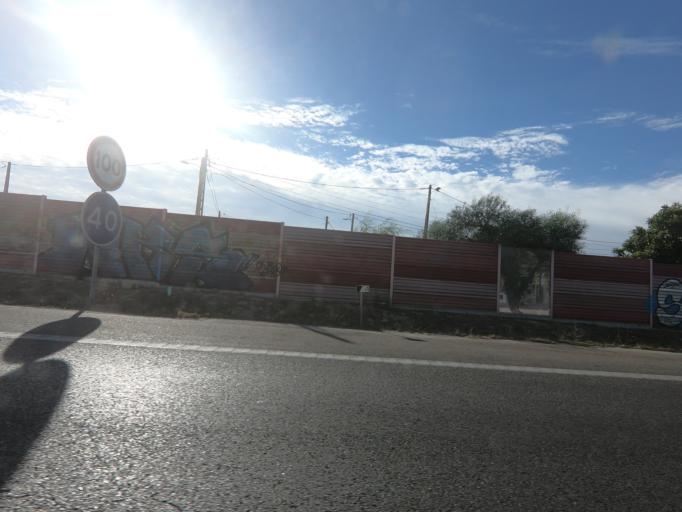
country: PT
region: Setubal
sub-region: Barreiro
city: Santo Antonio da Charneca
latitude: 38.6417
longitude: -9.0490
